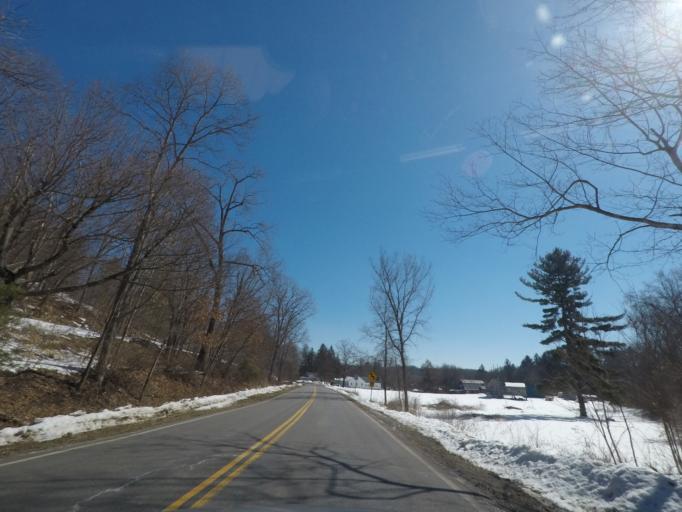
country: US
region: New York
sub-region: Saratoga County
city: Schuylerville
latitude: 43.1201
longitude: -73.5717
